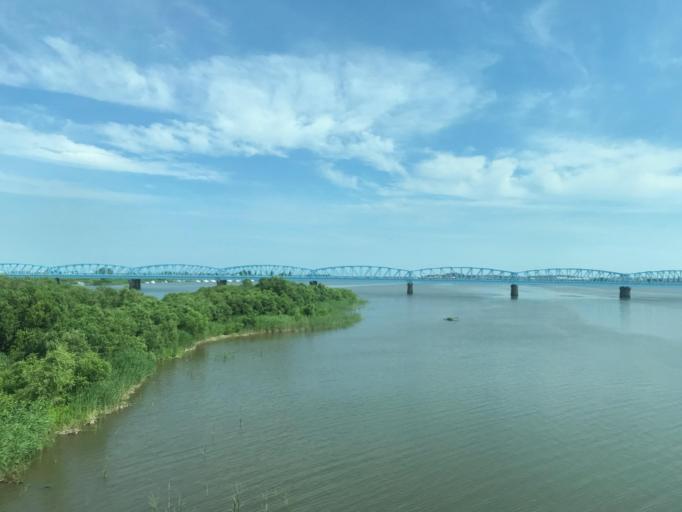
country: JP
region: Niigata
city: Kameda-honcho
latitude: 37.9195
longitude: 139.1463
